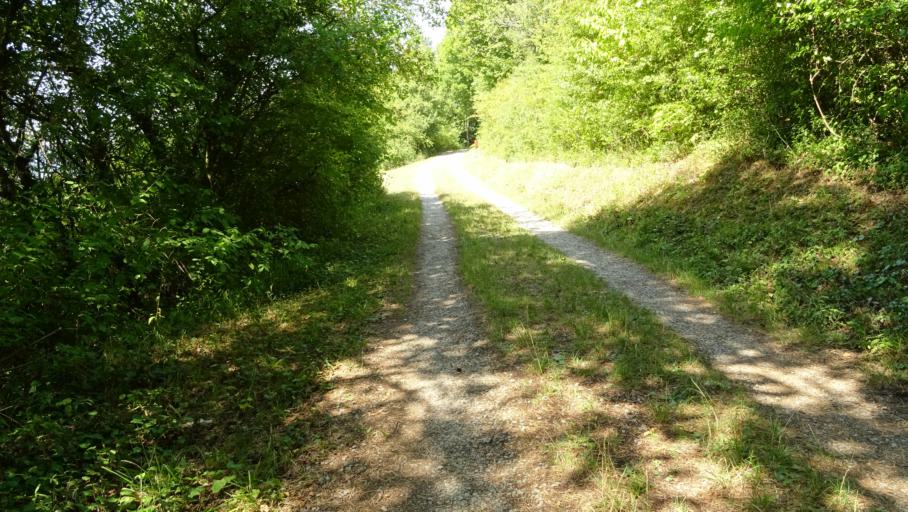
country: DE
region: Baden-Wuerttemberg
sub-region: Karlsruhe Region
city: Obrigheim
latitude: 49.3498
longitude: 9.1183
